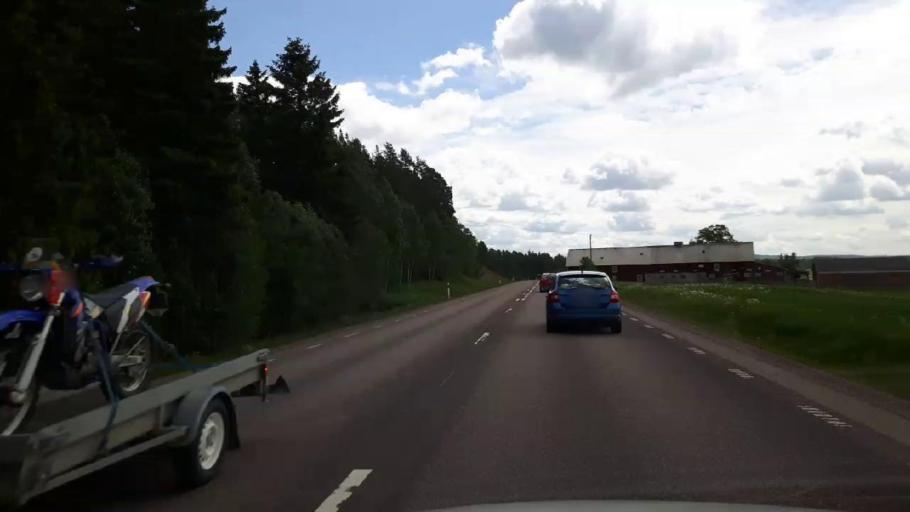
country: SE
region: Dalarna
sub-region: Saters Kommun
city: Saeter
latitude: 60.4375
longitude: 15.8219
